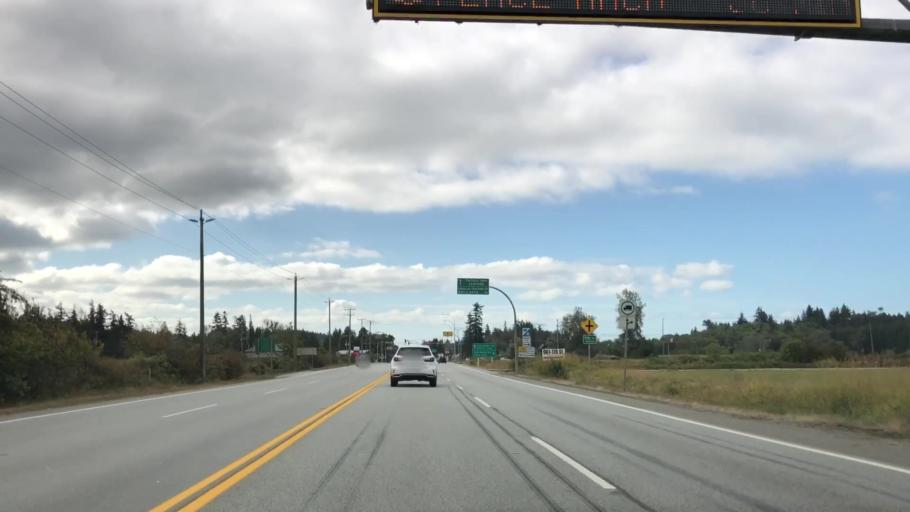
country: US
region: Washington
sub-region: Whatcom County
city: Blaine
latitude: 49.0194
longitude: -122.7353
